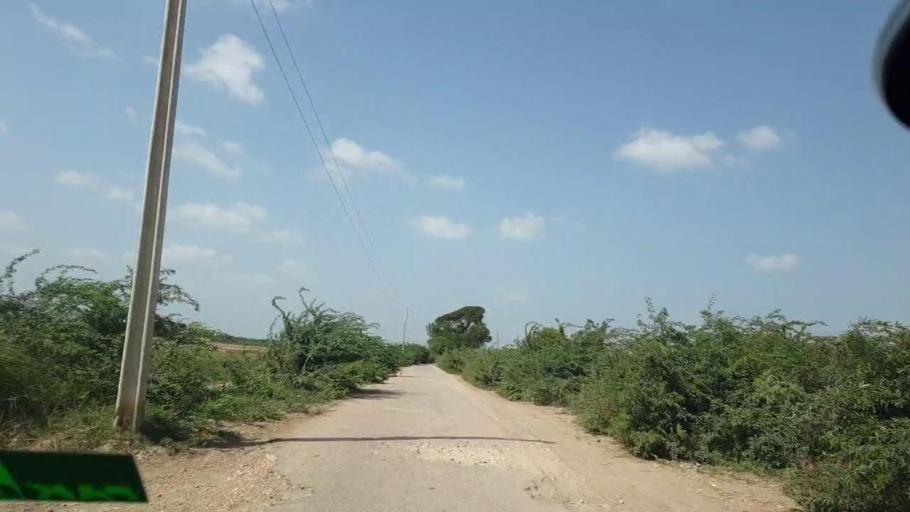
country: PK
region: Sindh
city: Naukot
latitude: 24.6345
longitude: 69.2272
